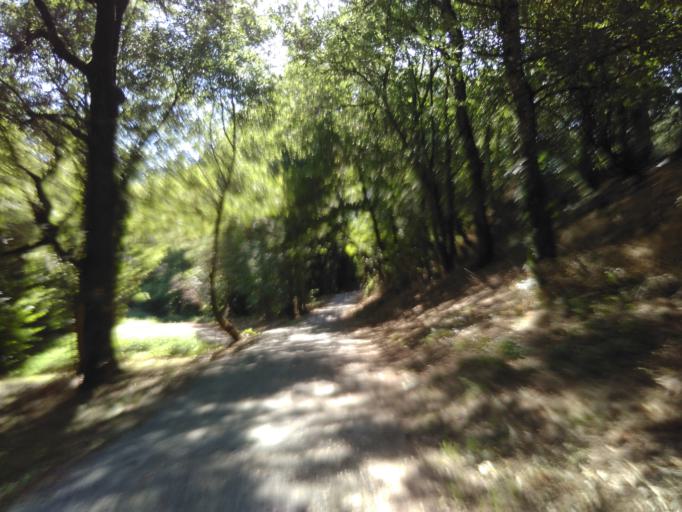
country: FR
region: Pays de la Loire
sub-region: Departement de la Vendee
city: La Chaize-le-Vicomte
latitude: 46.6689
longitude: -1.2955
